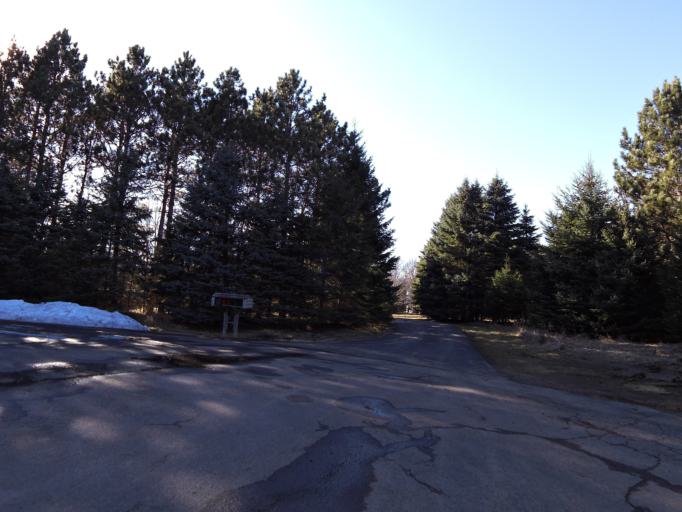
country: US
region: Minnesota
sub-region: Washington County
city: Lake Elmo
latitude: 44.9862
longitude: -92.8261
